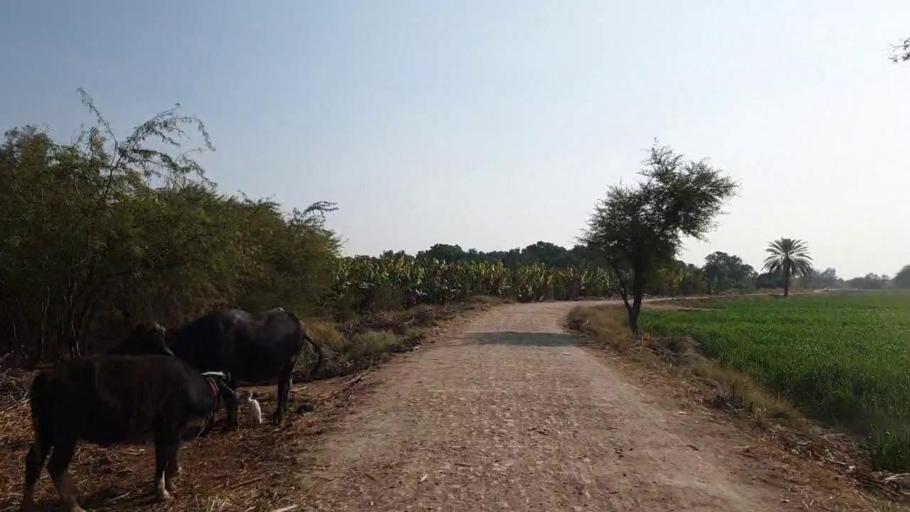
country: PK
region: Sindh
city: Tando Adam
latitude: 25.6809
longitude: 68.5662
